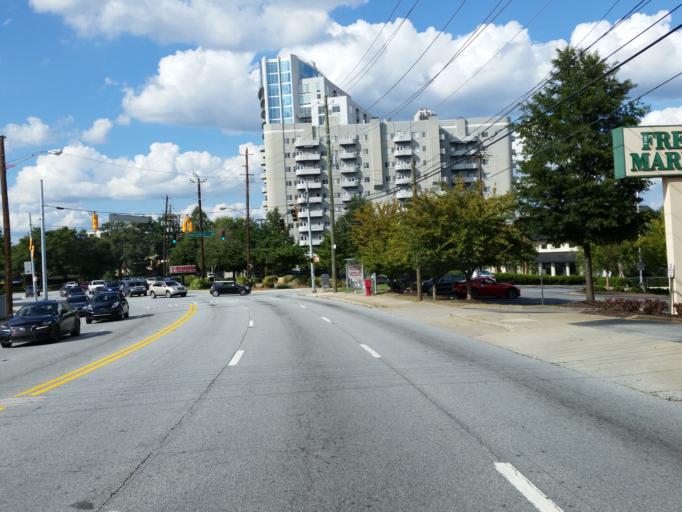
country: US
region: Georgia
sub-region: Fulton County
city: Atlanta
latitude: 33.8116
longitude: -84.3922
